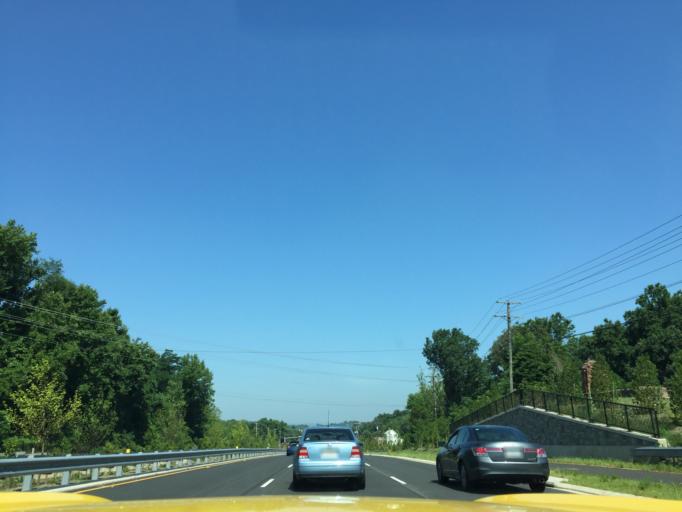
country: US
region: Virginia
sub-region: Fairfax County
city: Dranesville
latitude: 39.0033
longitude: -77.3506
